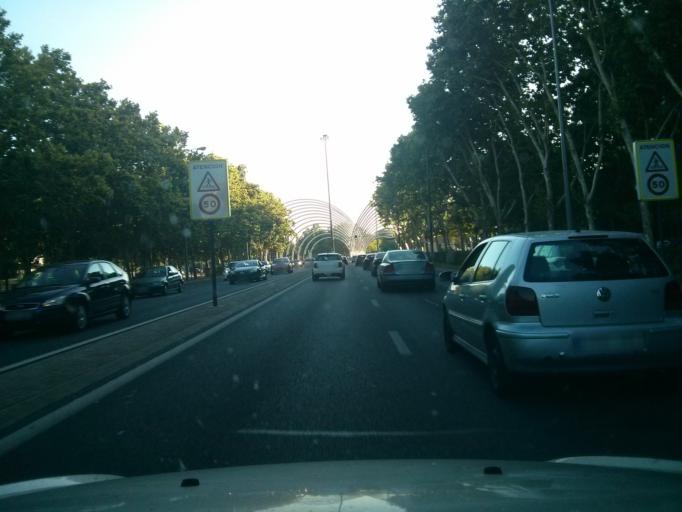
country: ES
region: Madrid
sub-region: Provincia de Madrid
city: Tetuan de las Victorias
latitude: 40.4826
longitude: -3.7030
